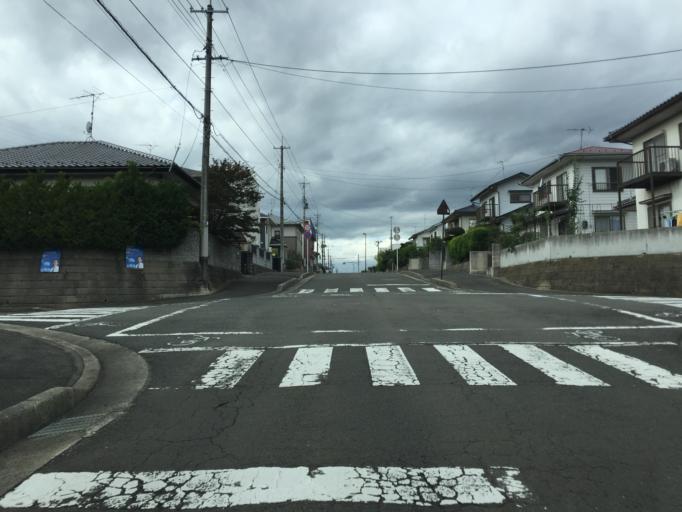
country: JP
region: Fukushima
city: Fukushima-shi
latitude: 37.7069
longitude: 140.4748
